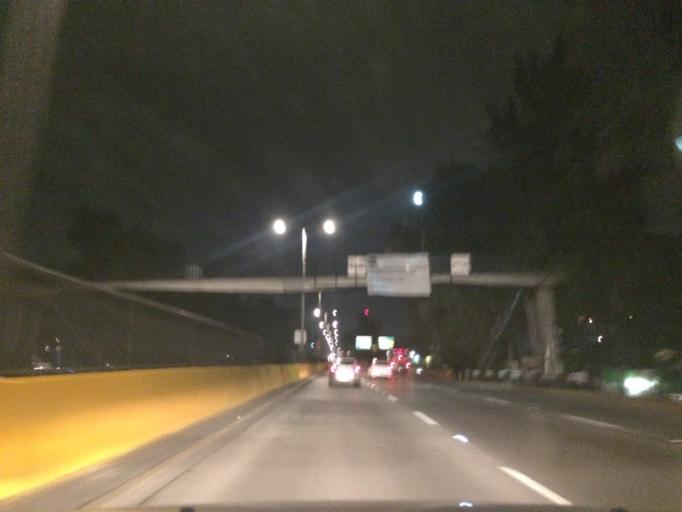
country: MX
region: Mexico City
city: Colonia Nativitas
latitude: 19.3678
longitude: -99.1257
